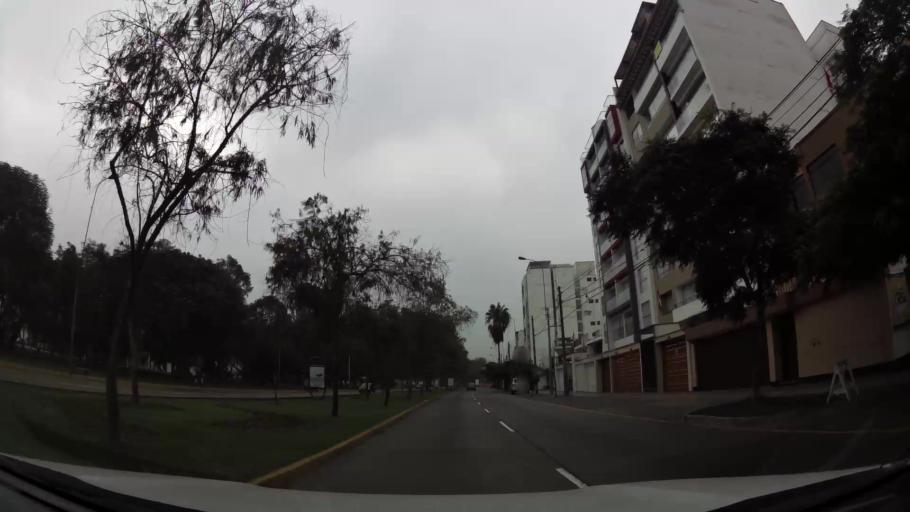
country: PE
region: Lima
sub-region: Lima
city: San Luis
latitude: -12.1006
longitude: -76.9967
